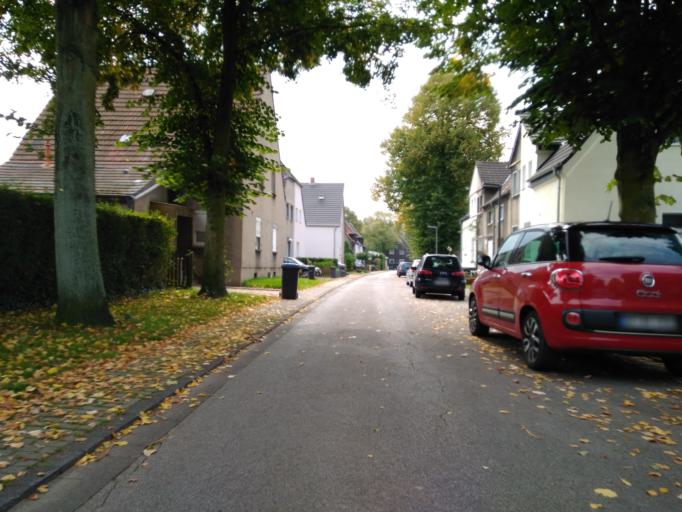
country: DE
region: North Rhine-Westphalia
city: Marl
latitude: 51.6026
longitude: 7.0547
